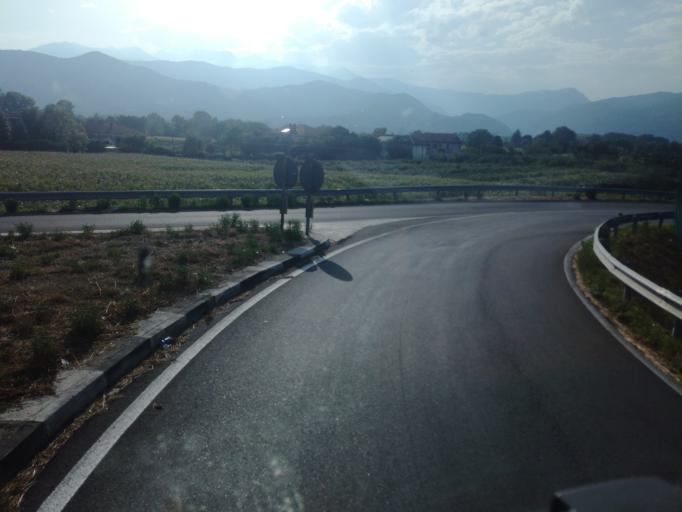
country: IT
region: Piedmont
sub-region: Provincia di Torino
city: Osasco
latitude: 44.8644
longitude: 7.3322
